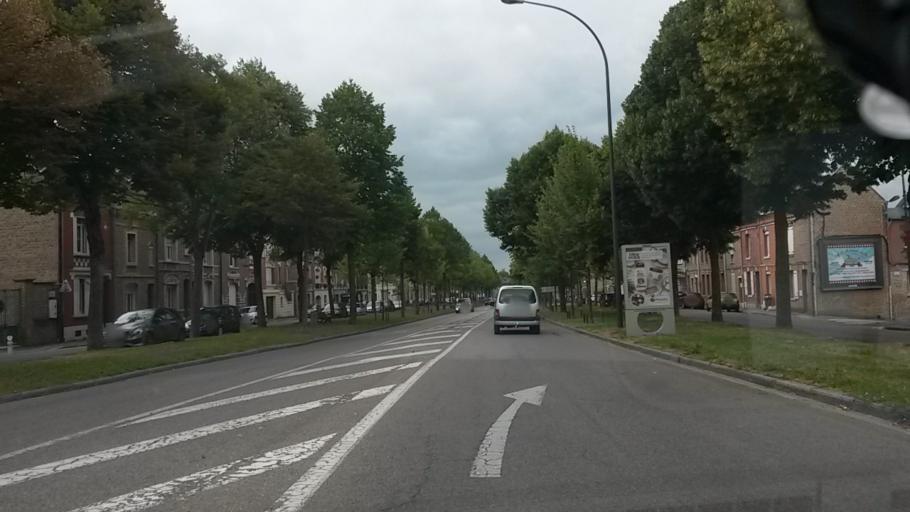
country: FR
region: Picardie
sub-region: Departement de la Somme
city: Amiens
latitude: 49.8845
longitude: 2.2814
